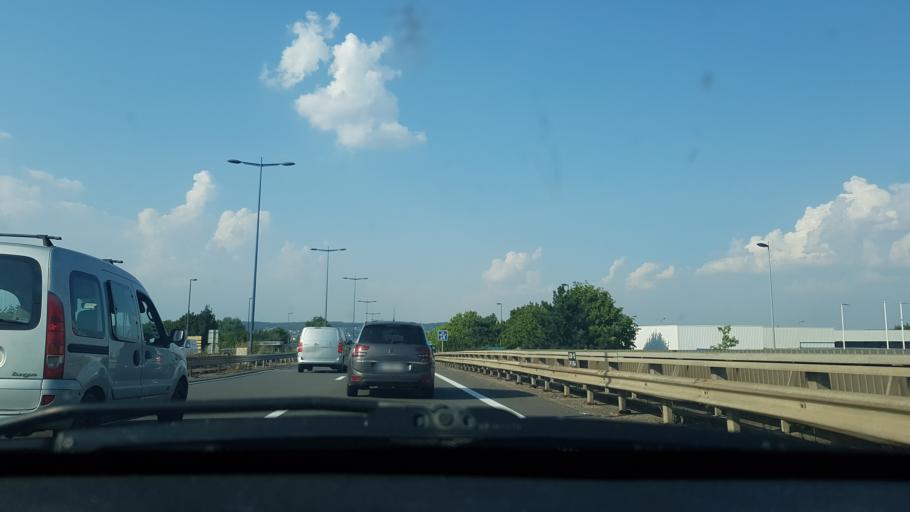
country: FR
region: Lorraine
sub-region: Departement de Meurthe-et-Moselle
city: Vandoeuvre-les-Nancy
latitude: 48.6609
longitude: 6.1874
